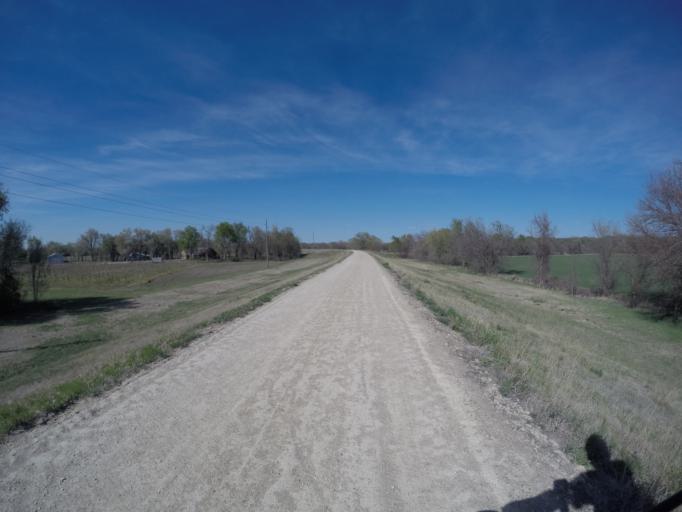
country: US
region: Kansas
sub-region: Saline County
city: Salina
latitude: 38.8132
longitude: -97.5834
